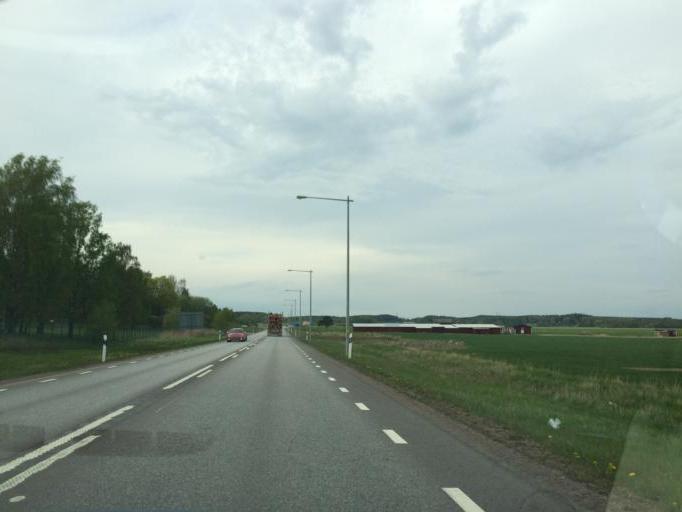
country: SE
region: Vaestmanland
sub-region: Kopings Kommun
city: Koping
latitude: 59.5235
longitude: 15.9649
